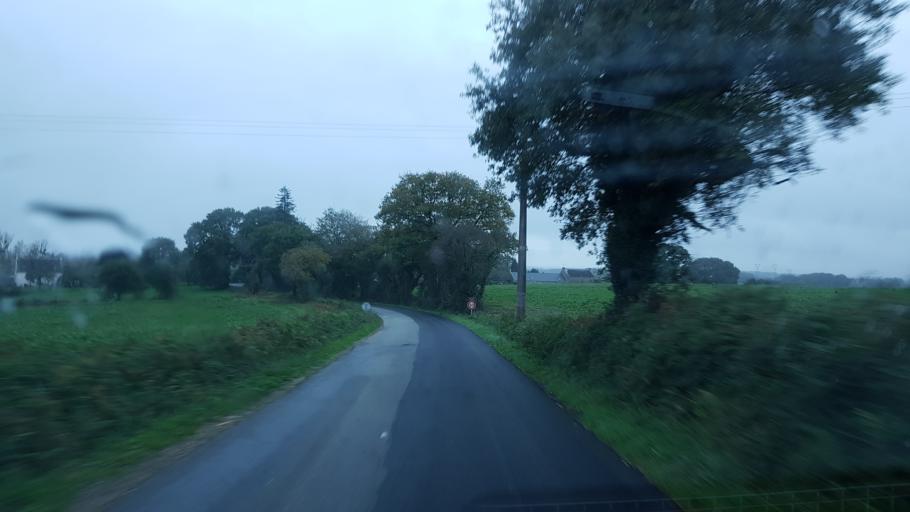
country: FR
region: Brittany
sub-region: Departement du Morbihan
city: Trefflean
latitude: 47.6644
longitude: -2.6198
